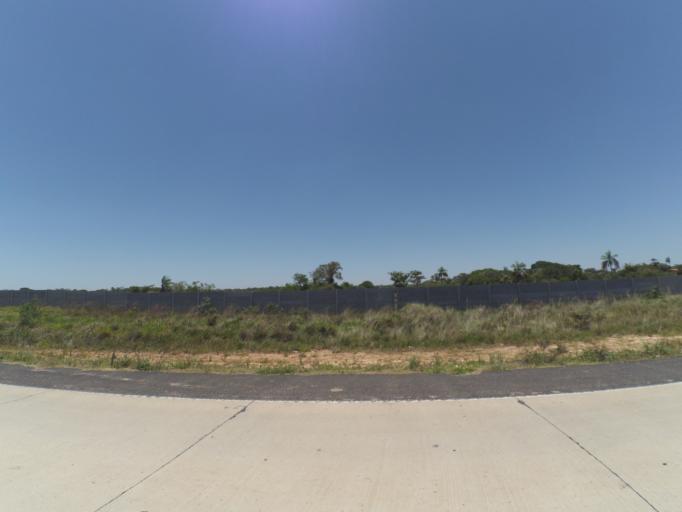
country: BO
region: Santa Cruz
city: Santa Cruz de la Sierra
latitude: -17.7878
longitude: -63.2734
